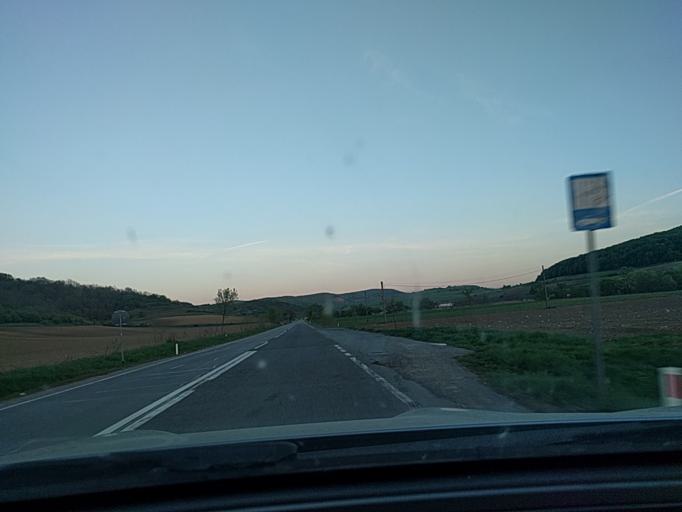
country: RO
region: Mures
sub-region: Comuna Nades
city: Nades
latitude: 46.3255
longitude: 24.7142
